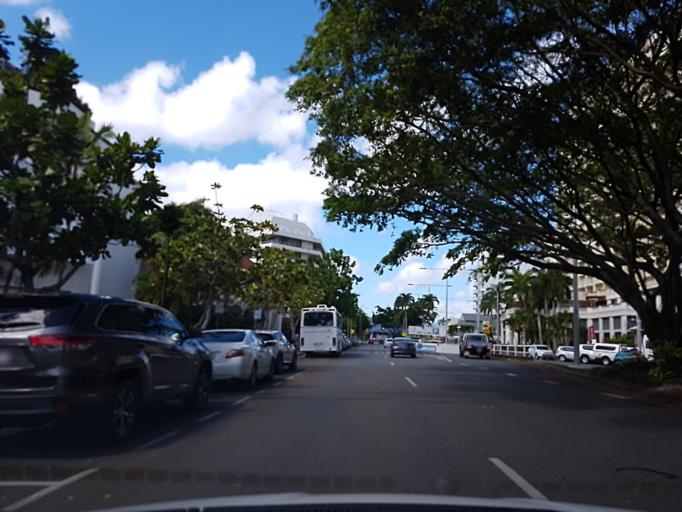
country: AU
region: Queensland
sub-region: Cairns
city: Cairns
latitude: -16.9232
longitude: 145.7786
